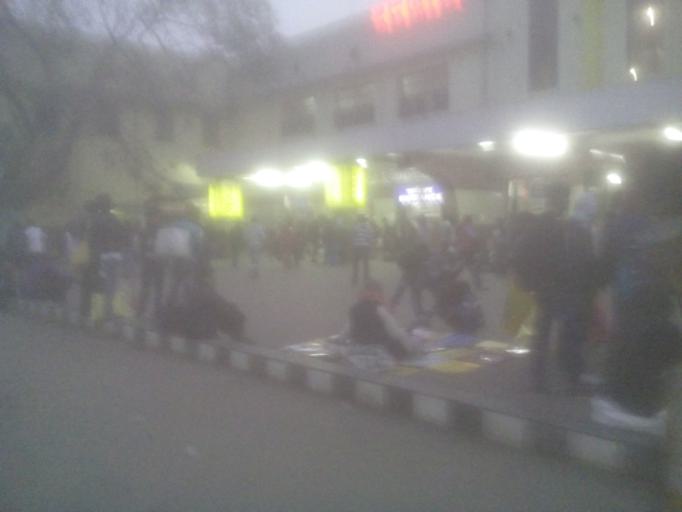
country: IN
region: Jharkhand
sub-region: Dhanbad
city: Dhanbad
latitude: 23.7928
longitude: 86.4280
